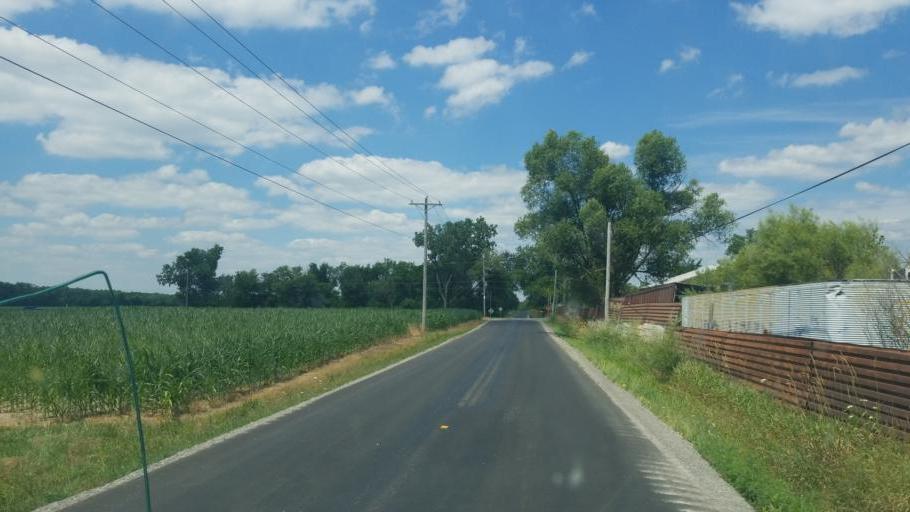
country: US
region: Ohio
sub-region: Williams County
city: Edgerton
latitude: 41.4467
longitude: -84.7103
